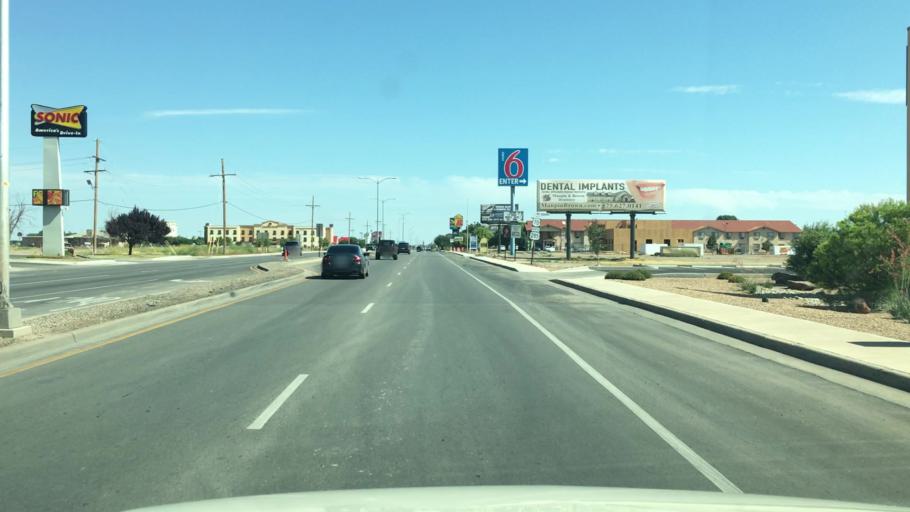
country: US
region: New Mexico
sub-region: Chaves County
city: Roswell
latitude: 33.4380
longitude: -104.5231
